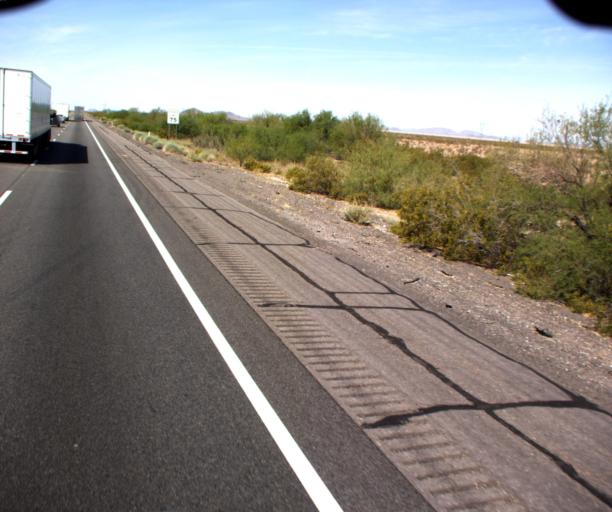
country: US
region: Arizona
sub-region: La Paz County
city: Salome
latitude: 33.5713
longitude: -113.3666
